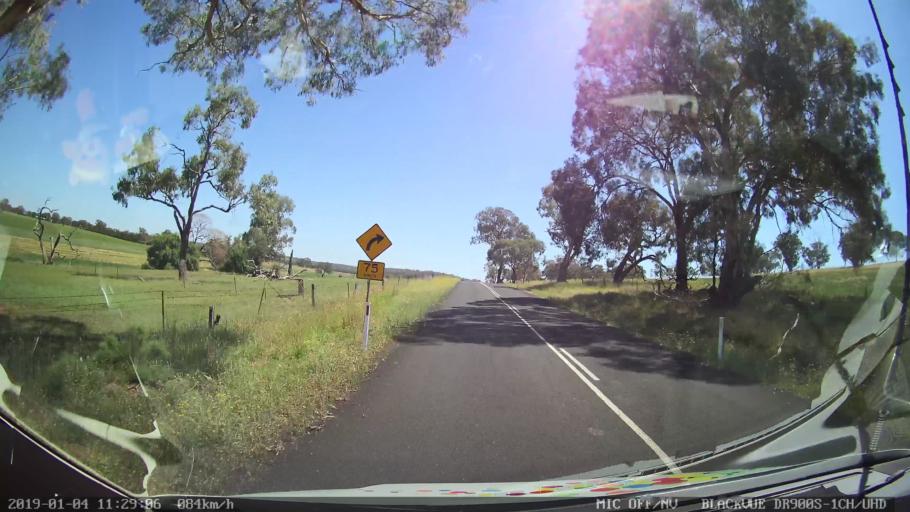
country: AU
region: New South Wales
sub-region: Cabonne
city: Molong
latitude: -33.0920
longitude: 148.7730
